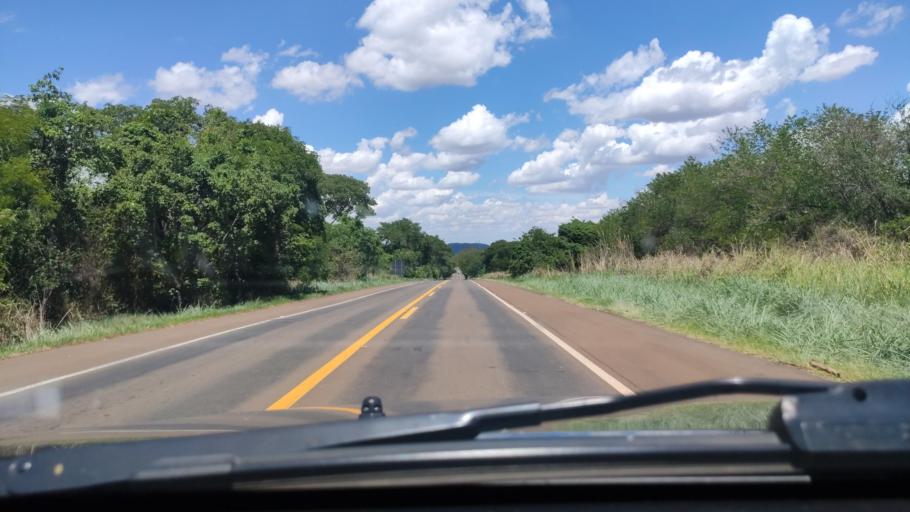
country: BR
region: Sao Paulo
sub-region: Boa Esperanca Do Sul
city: Boa Esperanca do Sul
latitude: -22.0696
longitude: -48.4105
